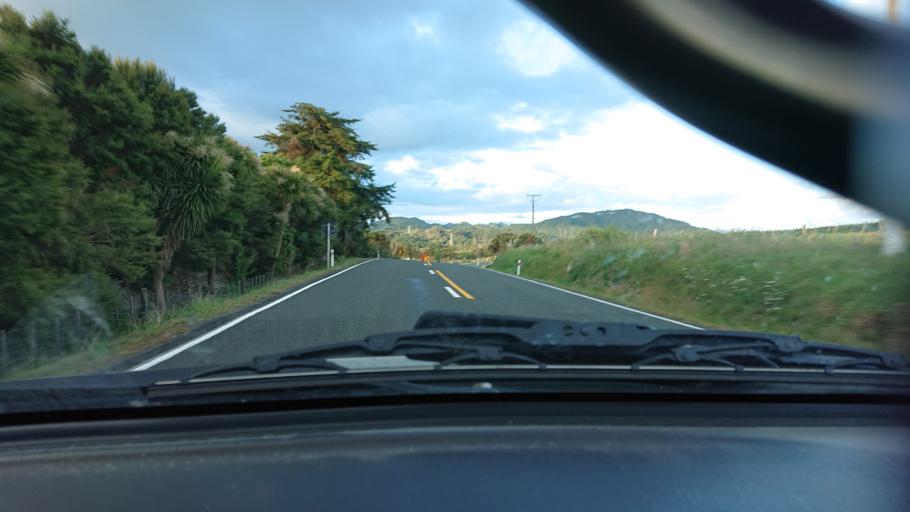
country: NZ
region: Auckland
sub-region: Auckland
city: Parakai
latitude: -36.5185
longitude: 174.4496
